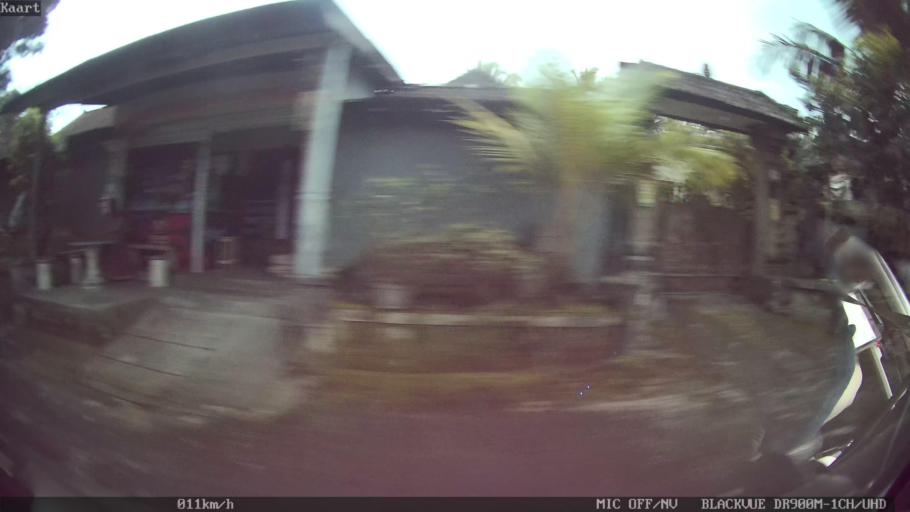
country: ID
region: Bali
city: Banjar Wangsian
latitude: -8.4394
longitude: 115.4267
